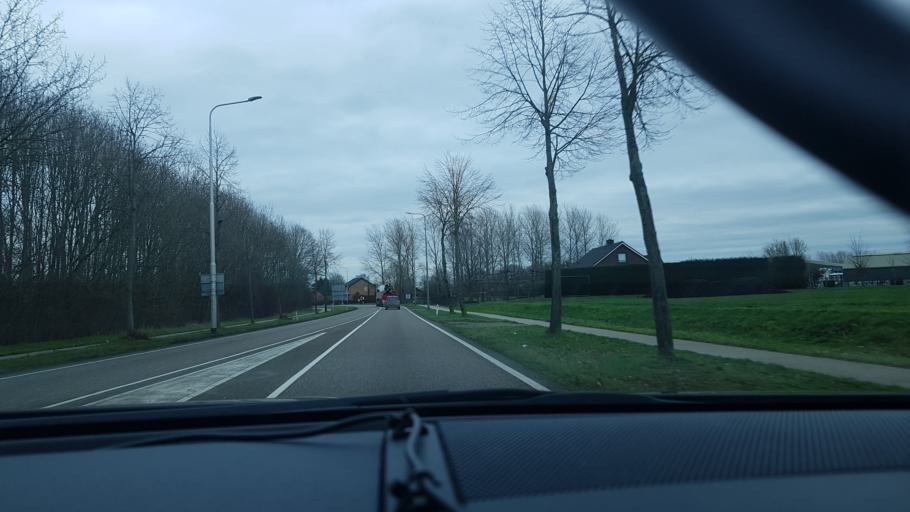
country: NL
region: Limburg
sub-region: Gemeente Leudal
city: Heythuysen
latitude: 51.2568
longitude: 5.9126
